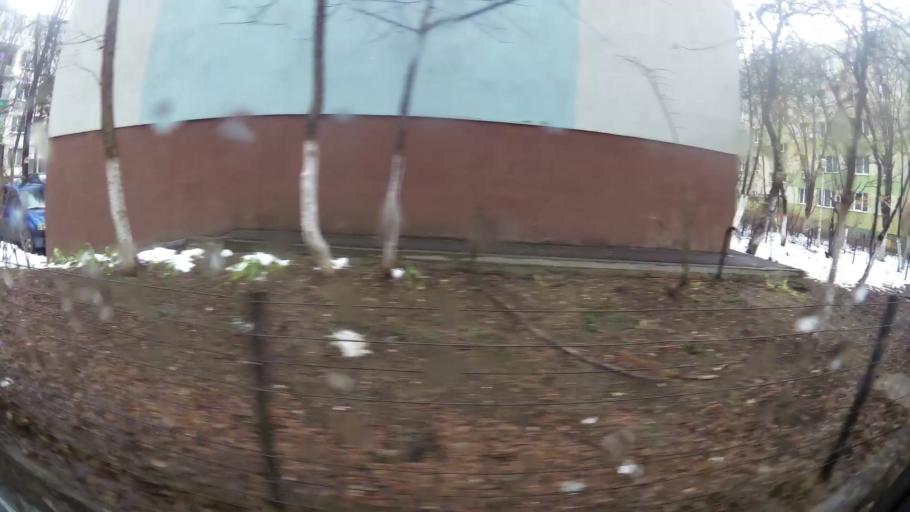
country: RO
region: Ilfov
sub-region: Comuna Chiajna
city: Rosu
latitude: 44.4149
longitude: 26.0200
